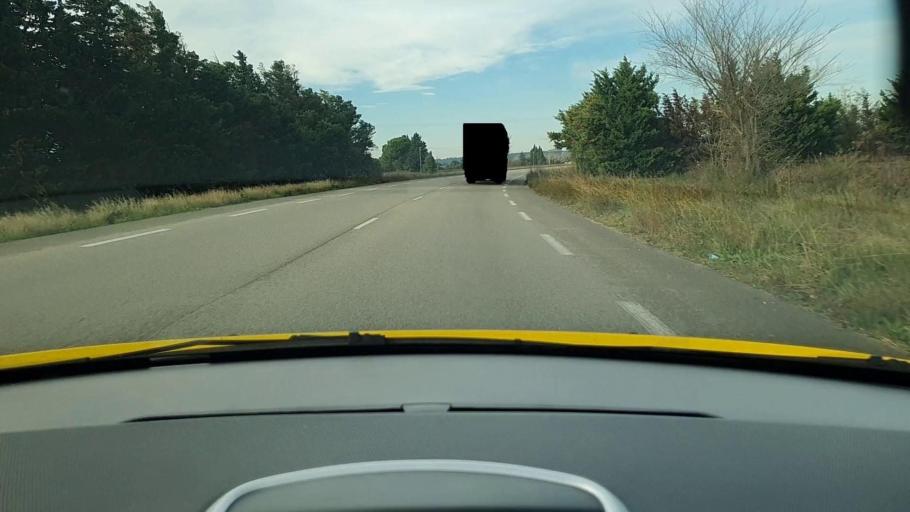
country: FR
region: Languedoc-Roussillon
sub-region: Departement du Gard
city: Beaucaire
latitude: 43.7925
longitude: 4.6167
